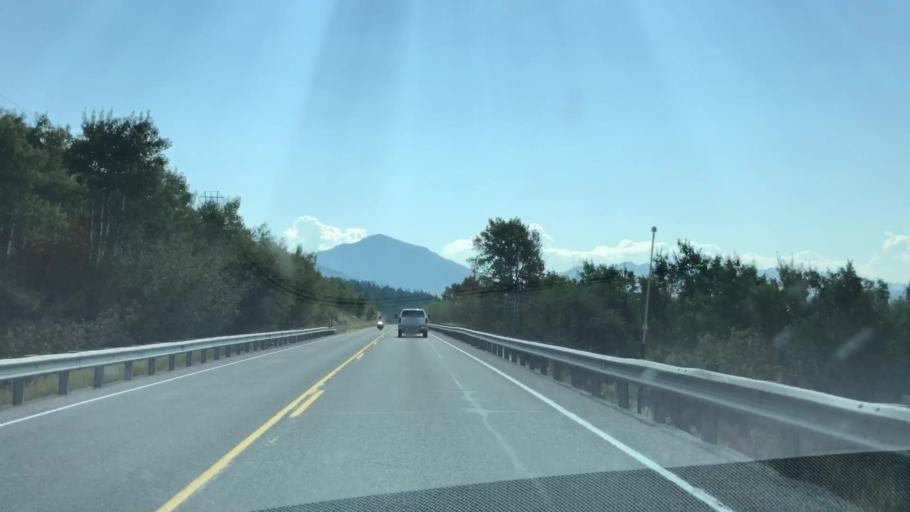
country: US
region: Wyoming
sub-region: Teton County
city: Hoback
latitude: 43.2074
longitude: -111.0546
